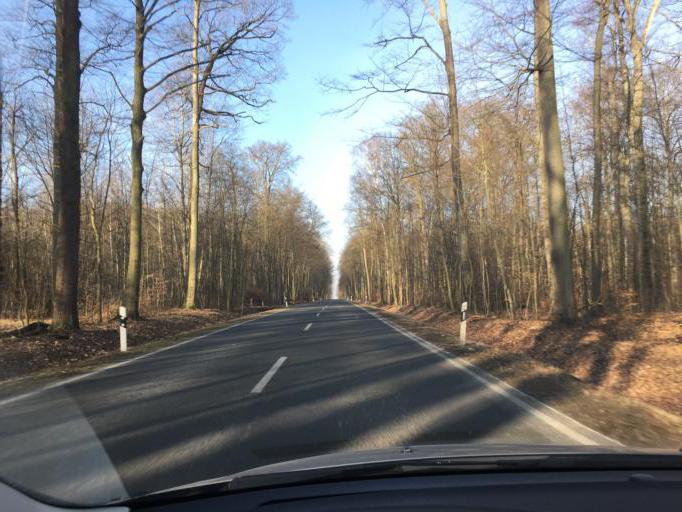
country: DE
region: Thuringia
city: Ziegelheim
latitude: 50.9822
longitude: 12.5409
